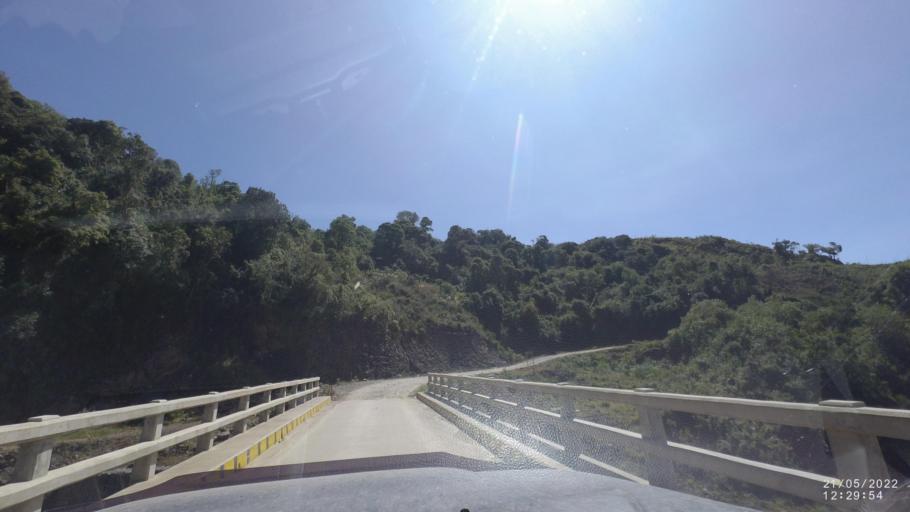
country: BO
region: Cochabamba
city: Colomi
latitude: -17.2160
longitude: -65.9138
